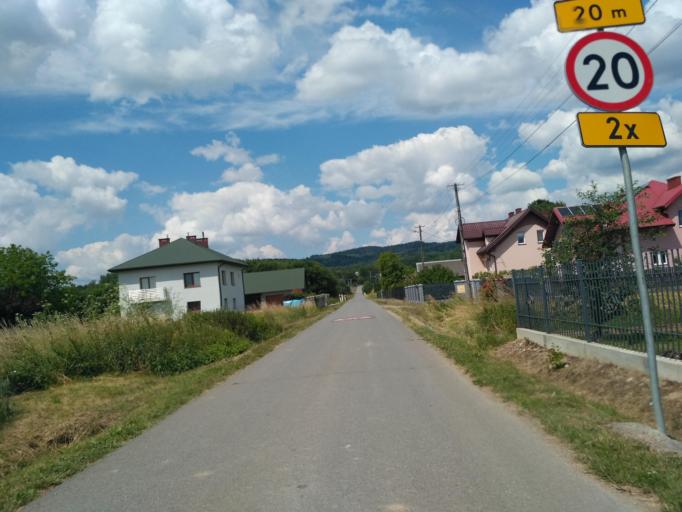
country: PL
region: Subcarpathian Voivodeship
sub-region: Powiat jasielski
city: Kolaczyce
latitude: 49.8043
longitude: 21.4124
